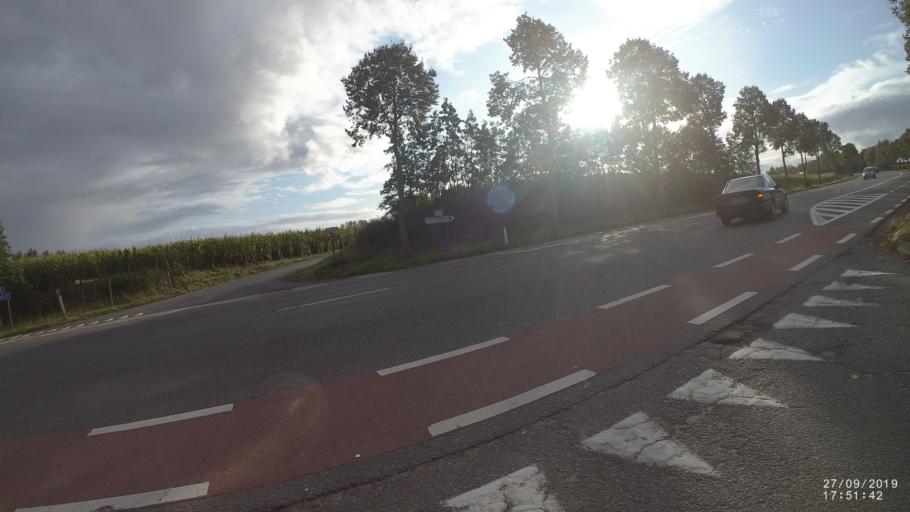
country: BE
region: Wallonia
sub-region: Province du Hainaut
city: Flobecq
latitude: 50.8194
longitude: 3.7134
